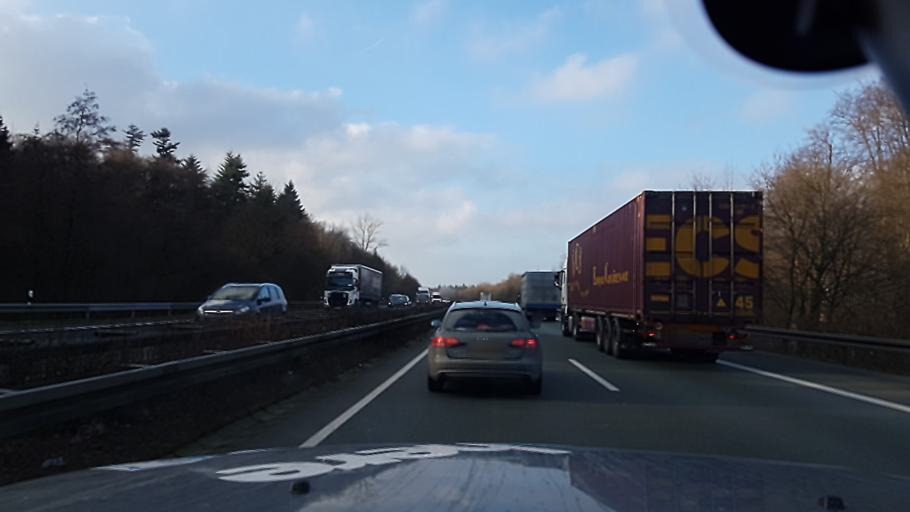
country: DE
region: North Rhine-Westphalia
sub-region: Regierungsbezirk Munster
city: Birgte
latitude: 52.2840
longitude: 7.6285
